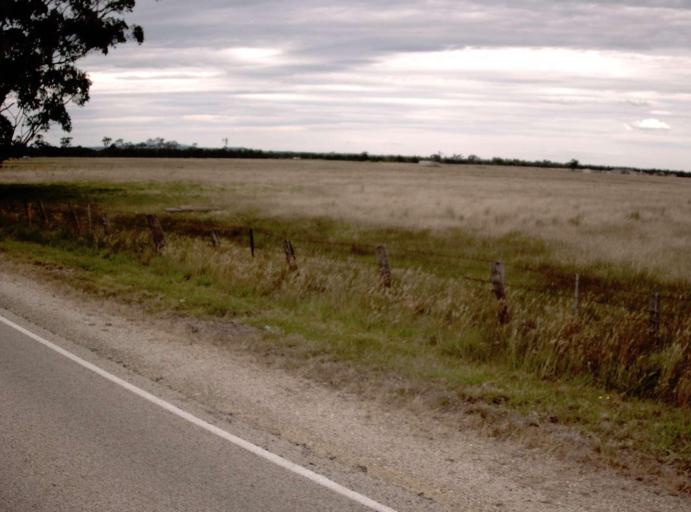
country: AU
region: Victoria
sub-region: East Gippsland
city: Bairnsdale
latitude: -37.8543
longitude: 147.5648
